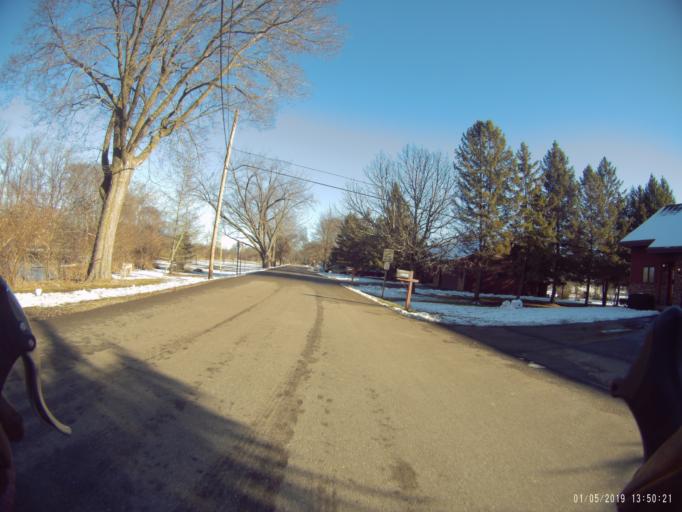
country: US
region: Wisconsin
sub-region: Dane County
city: Madison
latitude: 43.0447
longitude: -89.4151
